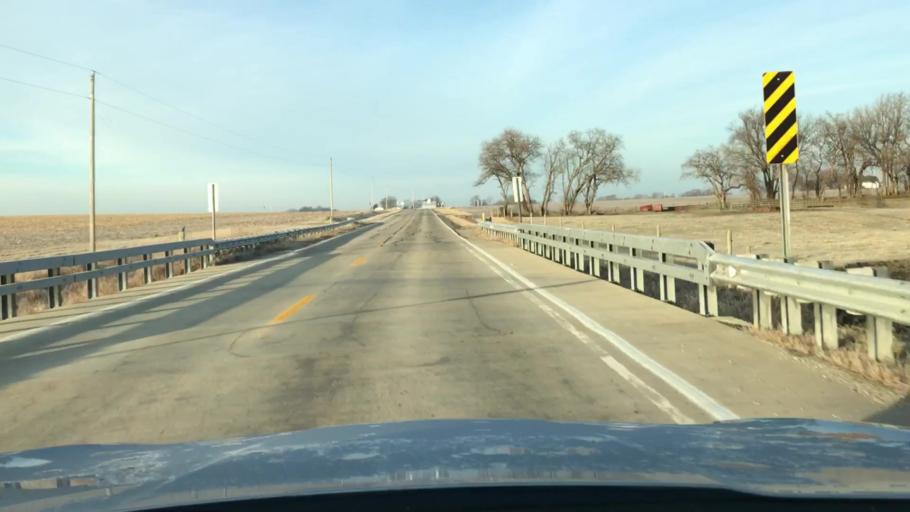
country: US
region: Illinois
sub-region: McLean County
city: Hudson
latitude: 40.6276
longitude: -88.9418
